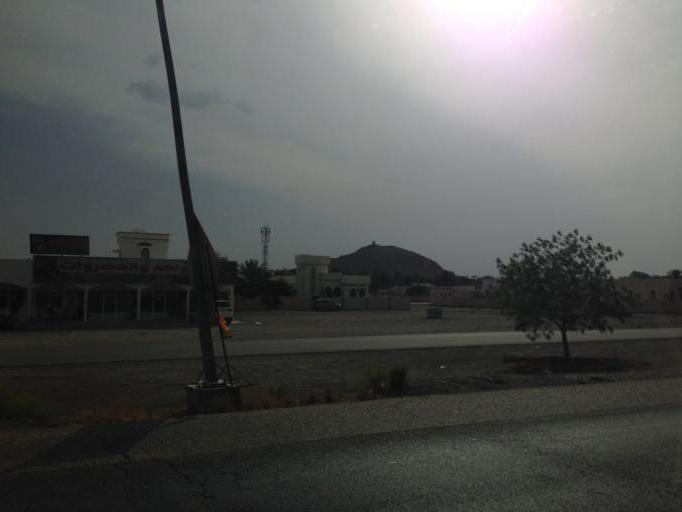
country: OM
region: Ash Sharqiyah
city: Al Qabil
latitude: 22.5807
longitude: 58.6895
